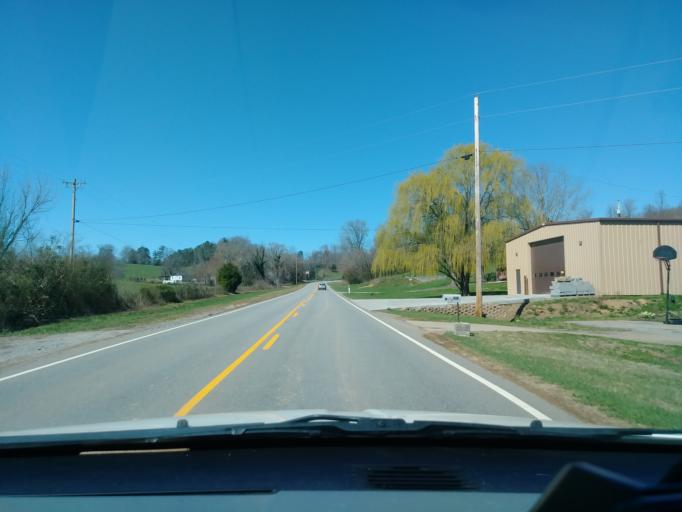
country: US
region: North Carolina
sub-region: Madison County
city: Marshall
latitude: 35.9056
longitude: -82.8847
